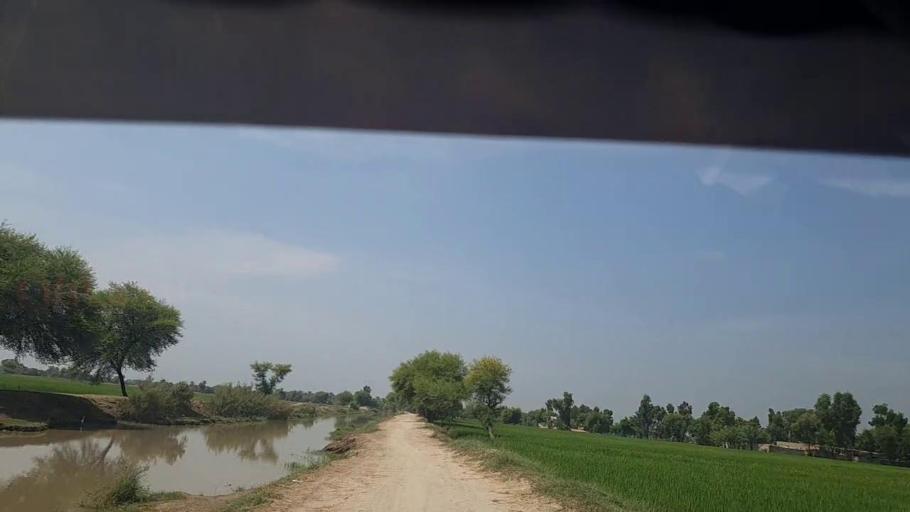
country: PK
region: Sindh
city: Thul
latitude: 28.2001
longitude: 68.7010
